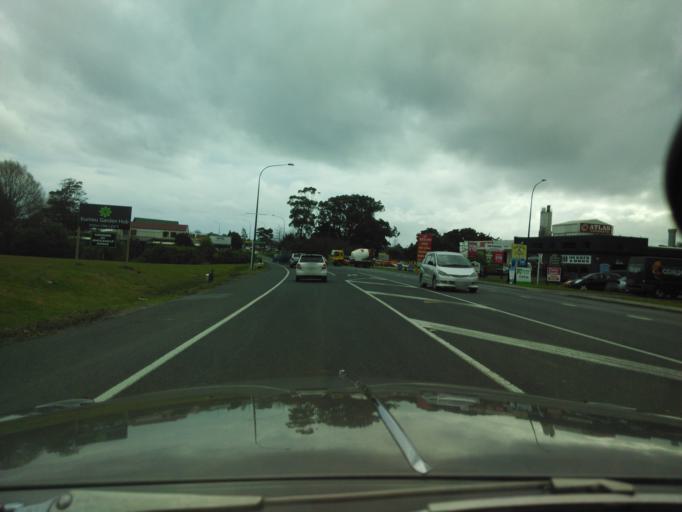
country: NZ
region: Auckland
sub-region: Auckland
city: Muriwai Beach
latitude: -36.7736
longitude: 174.5500
